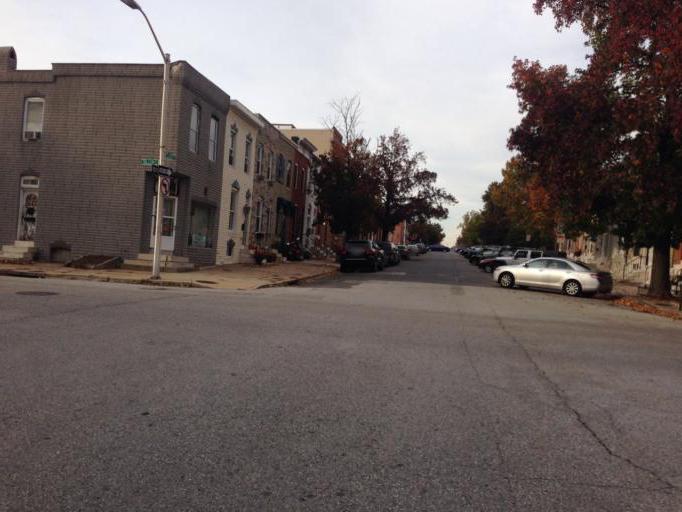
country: US
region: Maryland
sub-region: City of Baltimore
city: Baltimore
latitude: 39.2813
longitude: -76.5696
